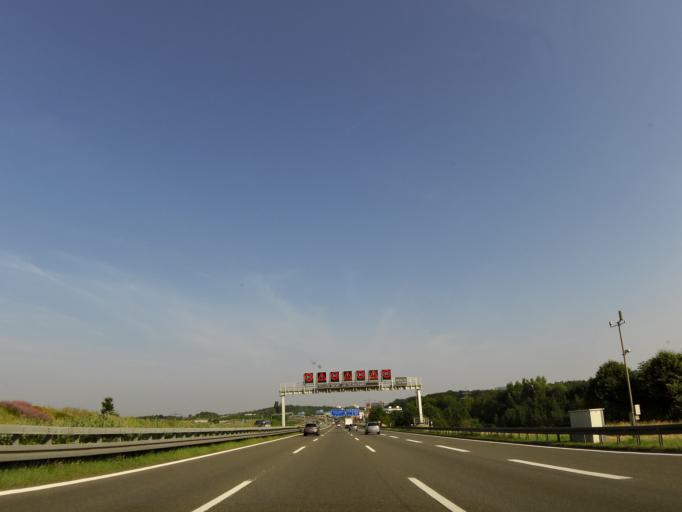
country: DE
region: Baden-Wuerttemberg
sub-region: Regierungsbezirk Stuttgart
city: Leinfelden-Echterdingen
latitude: 48.7012
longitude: 9.1808
